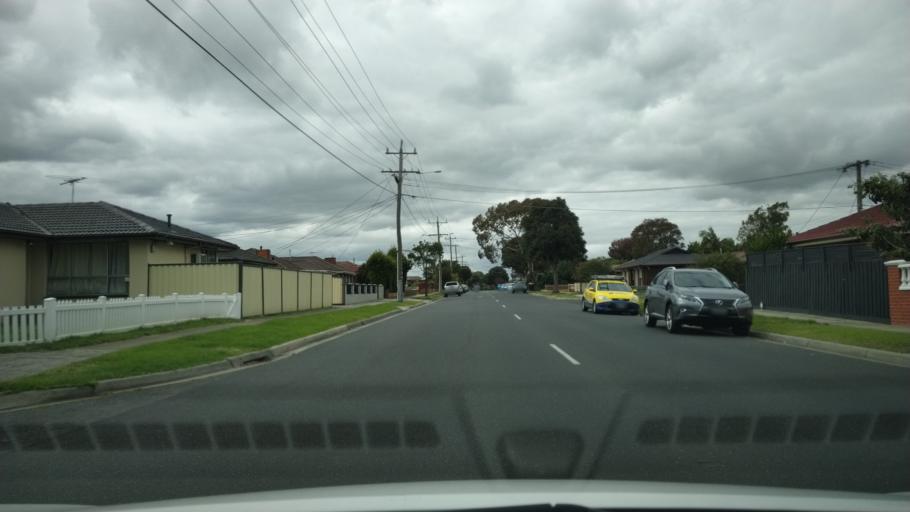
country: AU
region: Victoria
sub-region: Greater Dandenong
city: Keysborough
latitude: -37.9769
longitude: 145.1790
